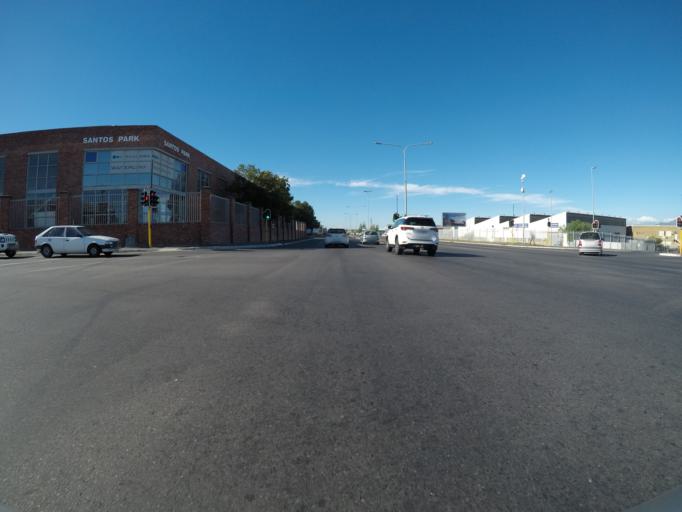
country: ZA
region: Western Cape
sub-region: City of Cape Town
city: Kraaifontein
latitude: -33.8995
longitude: 18.6703
